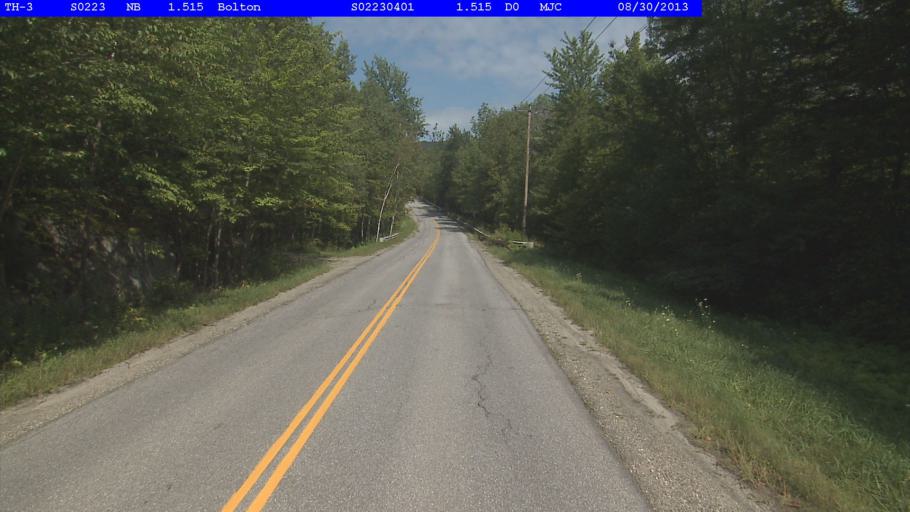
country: US
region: Vermont
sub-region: Washington County
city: Waterbury
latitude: 44.3919
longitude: -72.8760
